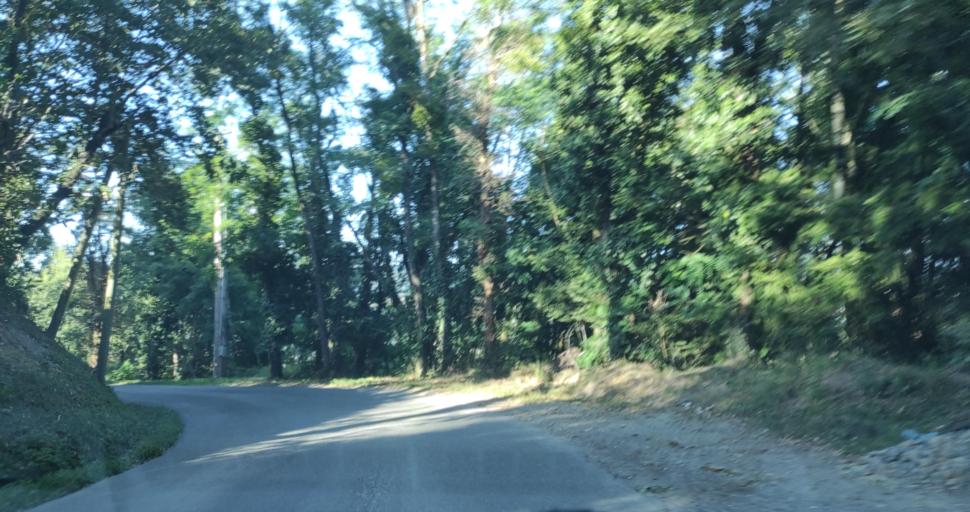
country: FR
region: Midi-Pyrenees
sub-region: Departement de l'Aveyron
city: Firmi
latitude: 44.5251
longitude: 2.3149
